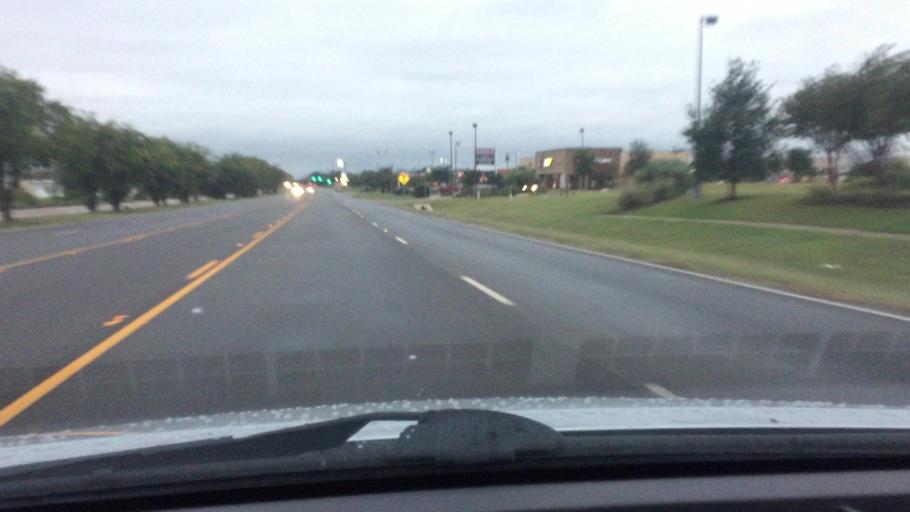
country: US
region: Texas
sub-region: Williamson County
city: Leander
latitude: 30.5626
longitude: -97.8462
